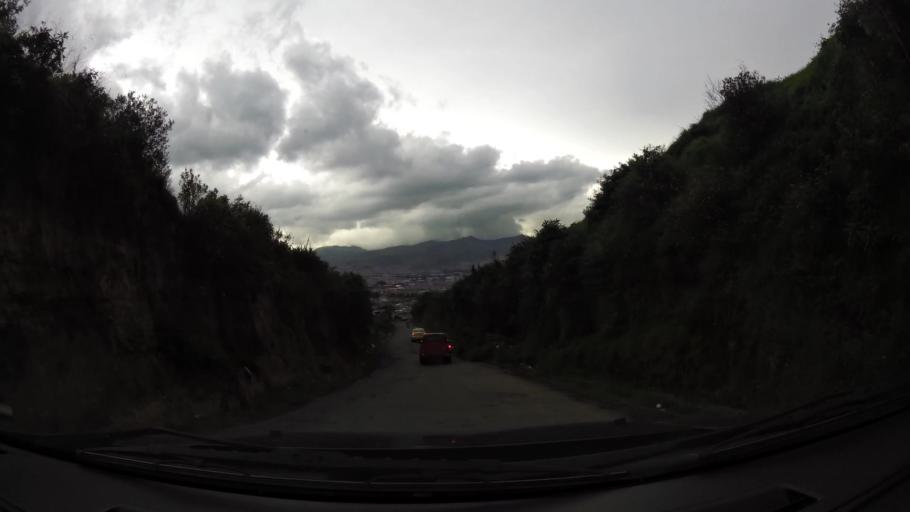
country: EC
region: Pichincha
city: Sangolqui
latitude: -0.3185
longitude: -78.5316
